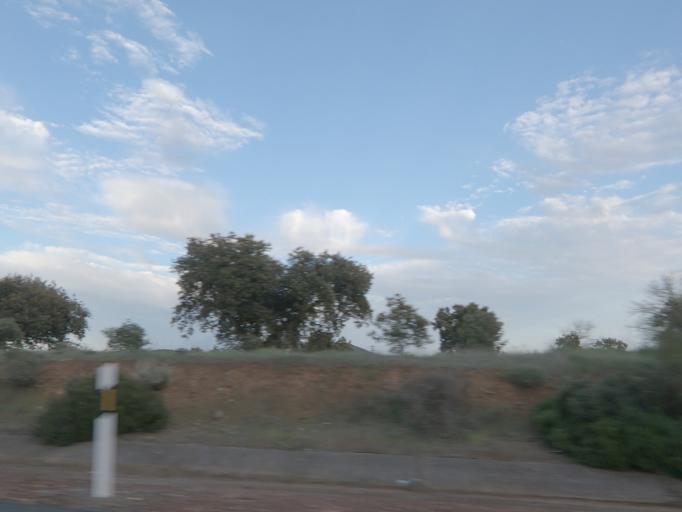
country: ES
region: Extremadura
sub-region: Provincia de Badajoz
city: Aljucen
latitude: 39.0584
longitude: -6.3224
